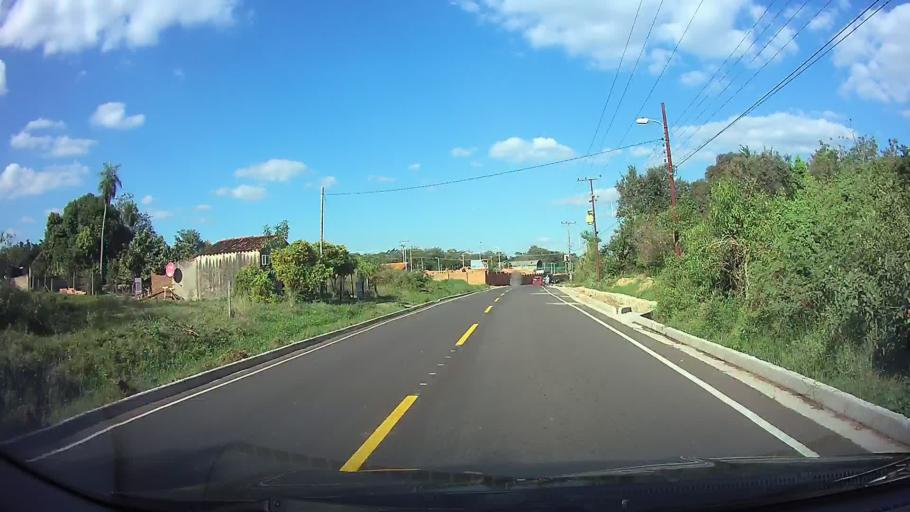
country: PY
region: Central
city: San Lorenzo
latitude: -25.2675
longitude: -57.4693
